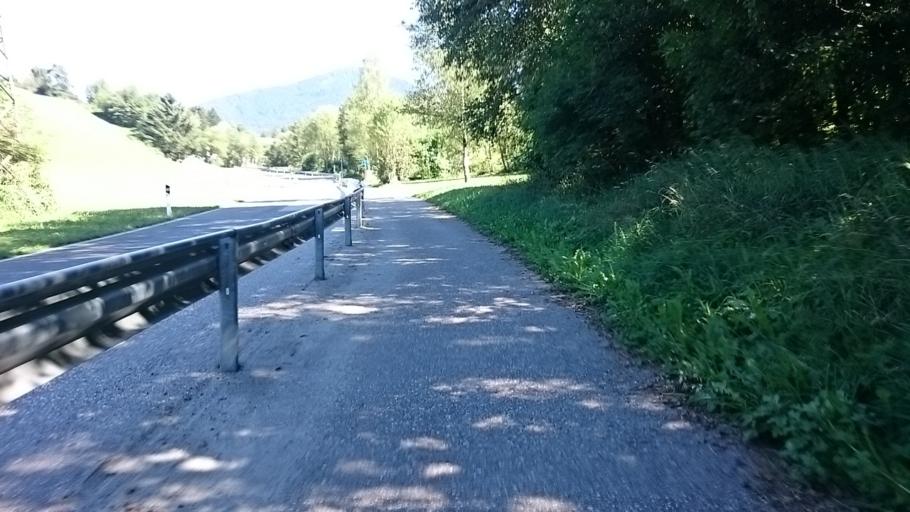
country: IT
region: Trentino-Alto Adige
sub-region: Bolzano
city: Valdaora di Mezzo
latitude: 46.7743
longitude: 12.0142
